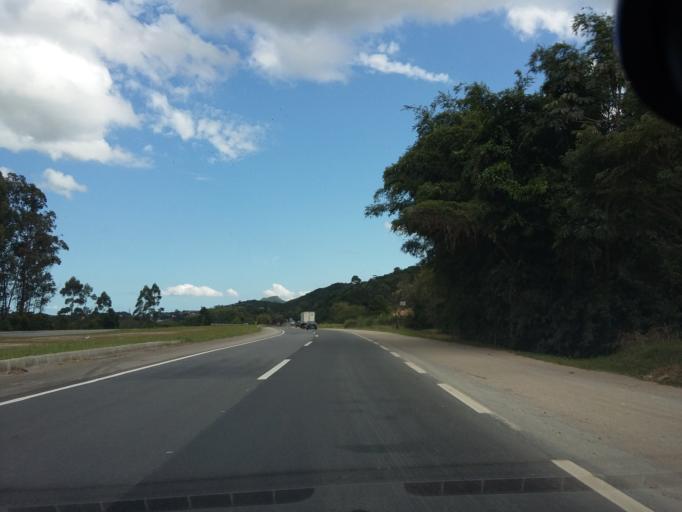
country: BR
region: Santa Catarina
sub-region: Tijucas
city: Tijucas
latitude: -27.3608
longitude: -48.6335
